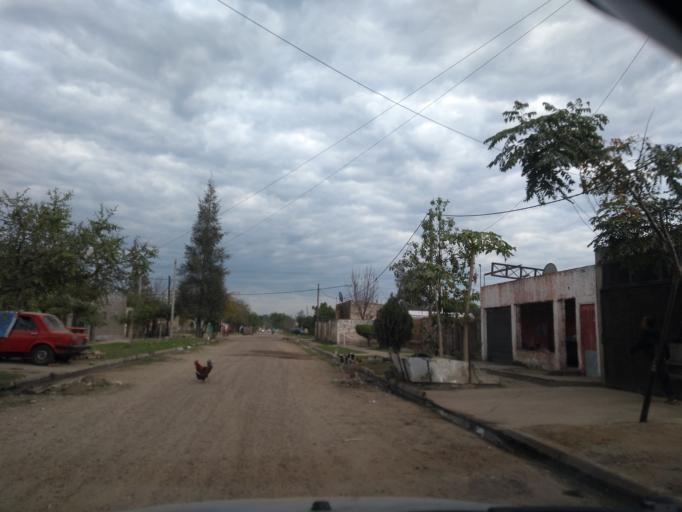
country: AR
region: Chaco
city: Resistencia
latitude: -27.4789
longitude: -58.9797
